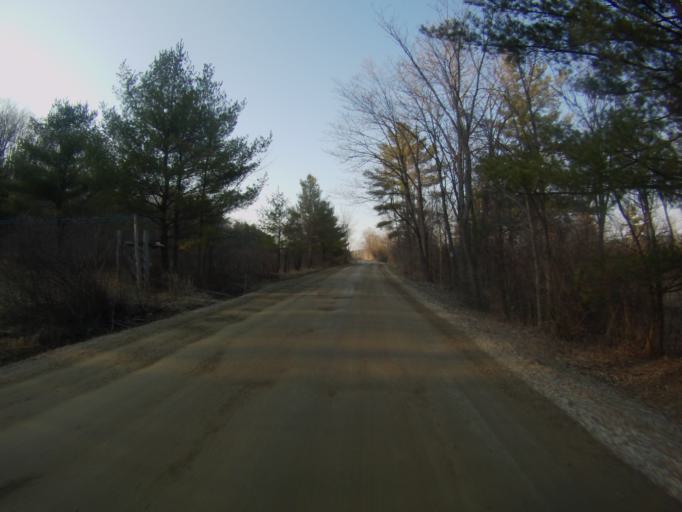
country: US
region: Vermont
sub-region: Addison County
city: Middlebury (village)
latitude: 44.0543
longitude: -73.1463
